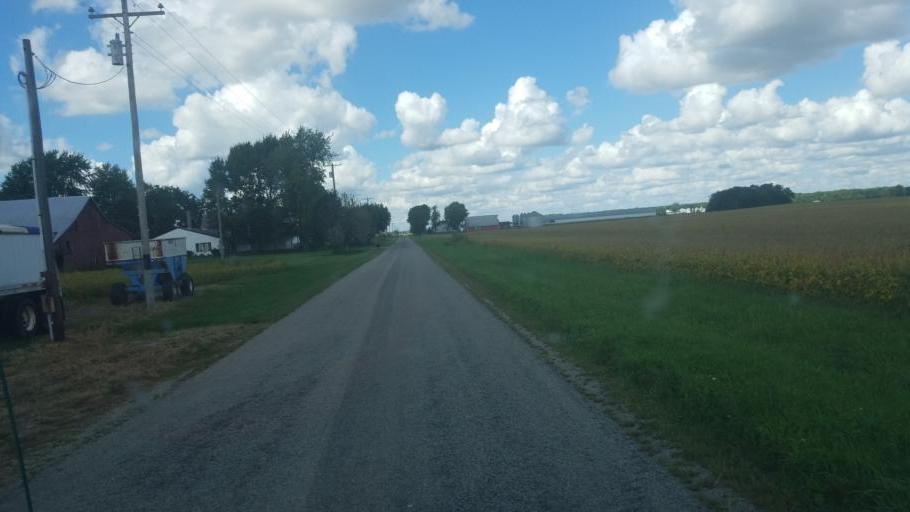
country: US
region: Ohio
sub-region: Union County
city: Richwood
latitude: 40.4499
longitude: -83.4936
